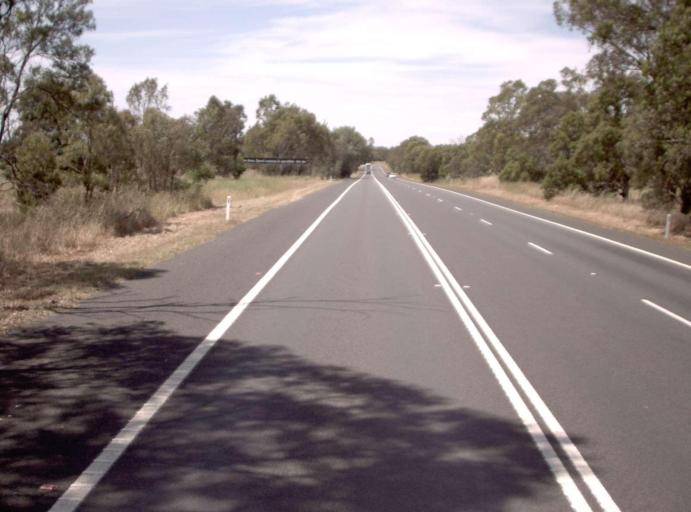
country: AU
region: Victoria
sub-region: Latrobe
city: Traralgon
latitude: -38.1635
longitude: 146.7028
